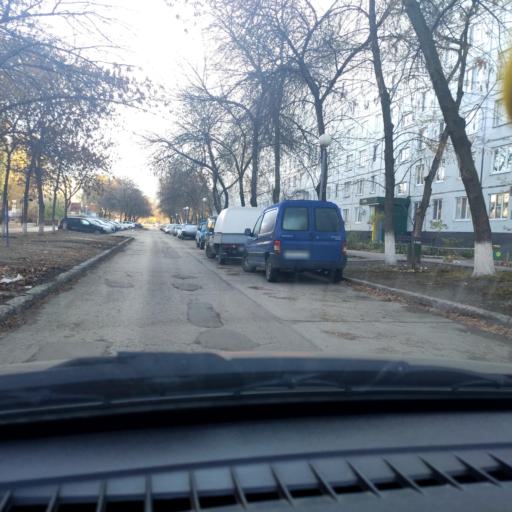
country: RU
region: Samara
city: Tol'yatti
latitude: 53.5110
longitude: 49.2887
